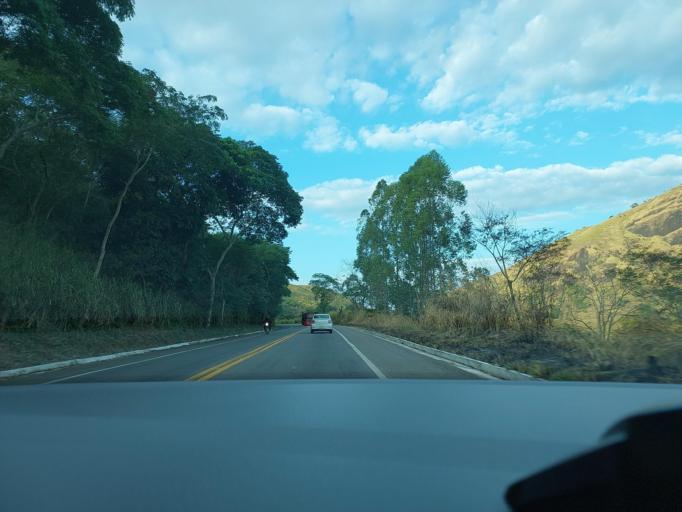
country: BR
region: Minas Gerais
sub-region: Muriae
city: Muriae
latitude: -21.1272
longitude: -42.2594
